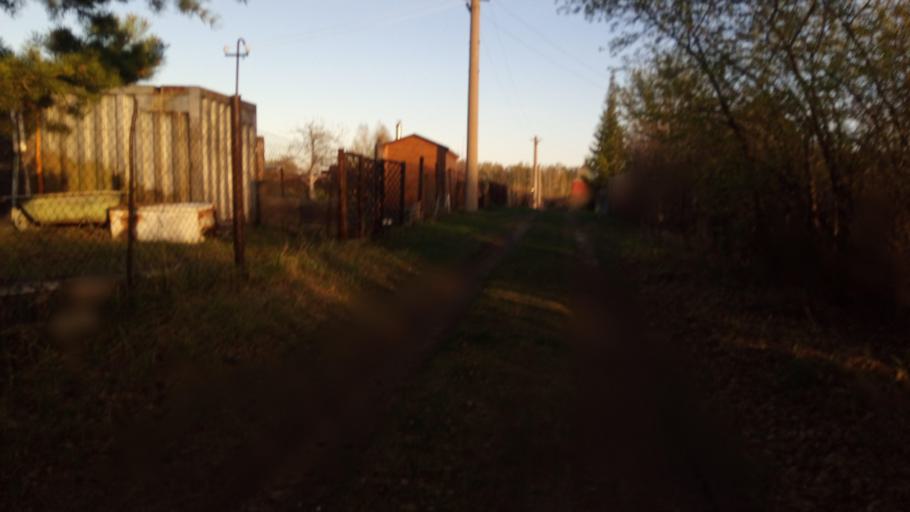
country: RU
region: Chelyabinsk
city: Timiryazevskiy
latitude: 54.9901
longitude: 60.8467
